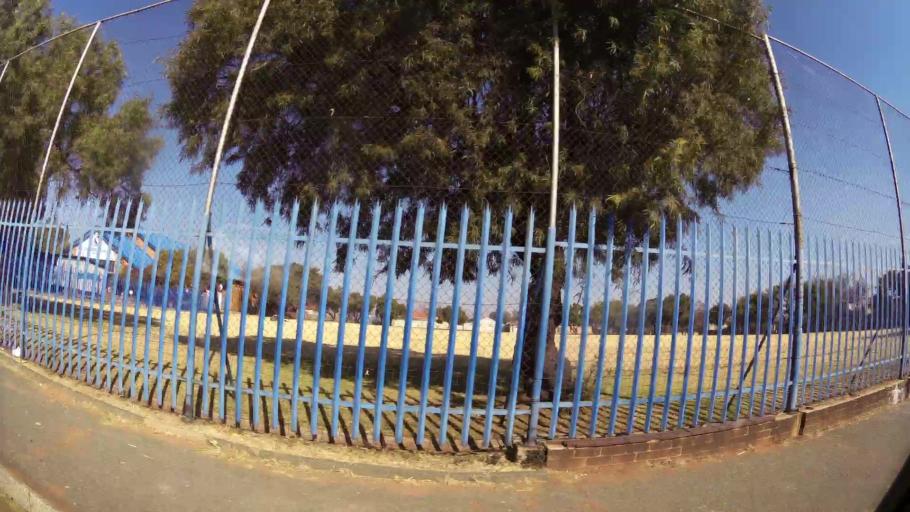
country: ZA
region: Gauteng
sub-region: City of Johannesburg Metropolitan Municipality
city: Johannesburg
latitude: -26.2586
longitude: 28.0516
